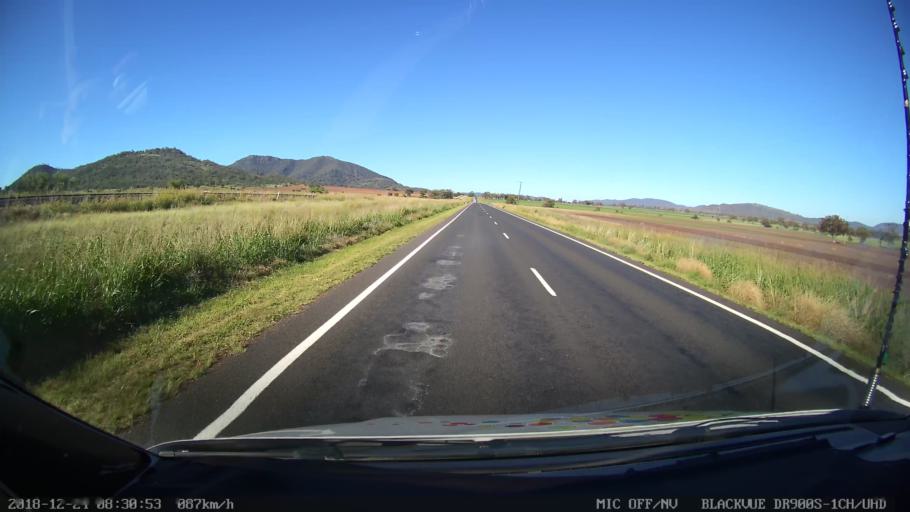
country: AU
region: New South Wales
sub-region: Tamworth Municipality
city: Phillip
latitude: -31.2700
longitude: 150.7190
